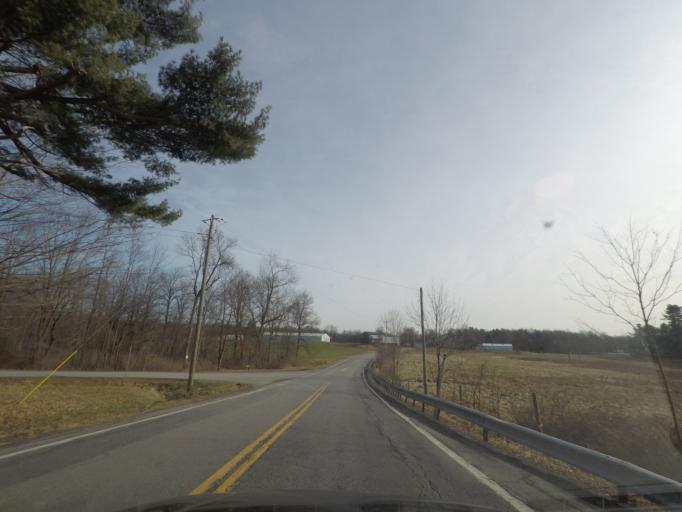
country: US
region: New York
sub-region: Saratoga County
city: Stillwater
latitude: 42.9879
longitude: -73.6900
